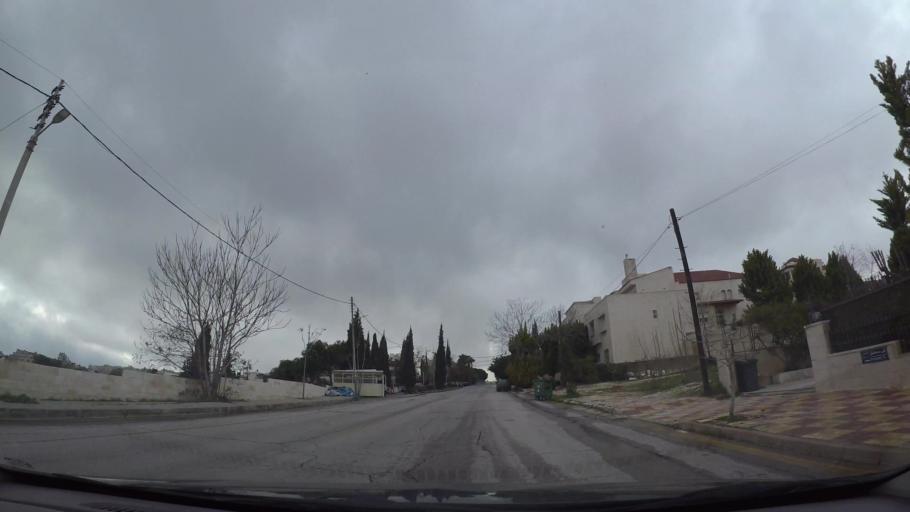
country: JO
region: Amman
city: Amman
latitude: 31.9441
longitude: 35.8979
